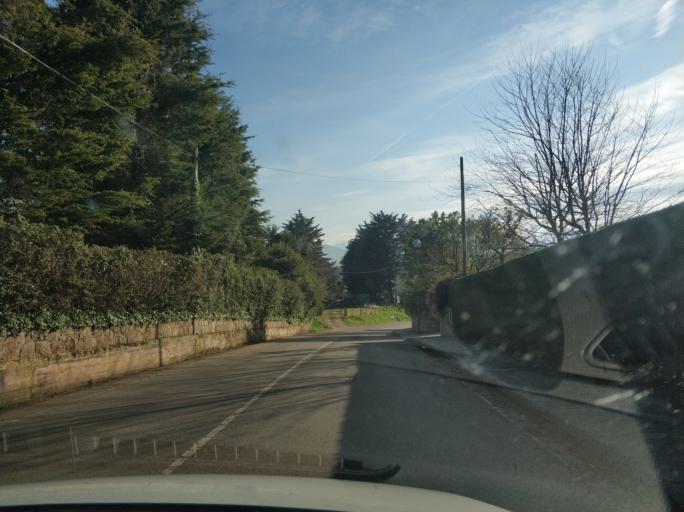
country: ES
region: Cantabria
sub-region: Provincia de Cantabria
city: Comillas
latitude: 43.3813
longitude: -4.3128
